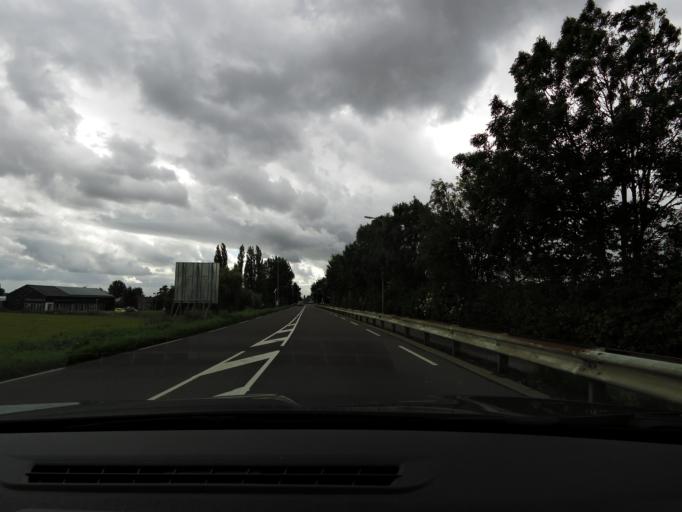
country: NL
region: South Holland
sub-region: Gemeente Oud-Beijerland
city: Oud-Beijerland
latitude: 51.8224
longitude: 4.4419
